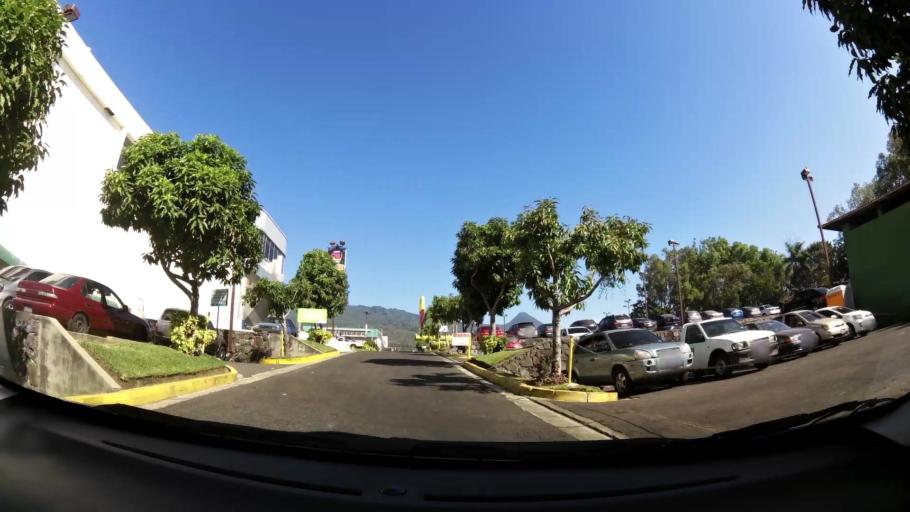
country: SV
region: La Libertad
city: Santa Tecla
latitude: 13.6784
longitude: -89.2745
